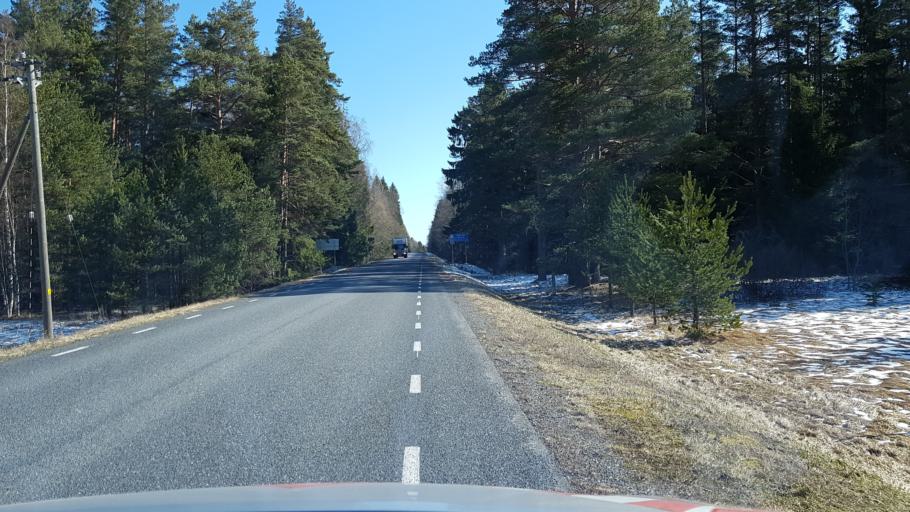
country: EE
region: Harju
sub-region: Loksa linn
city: Loksa
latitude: 59.5593
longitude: 25.8367
